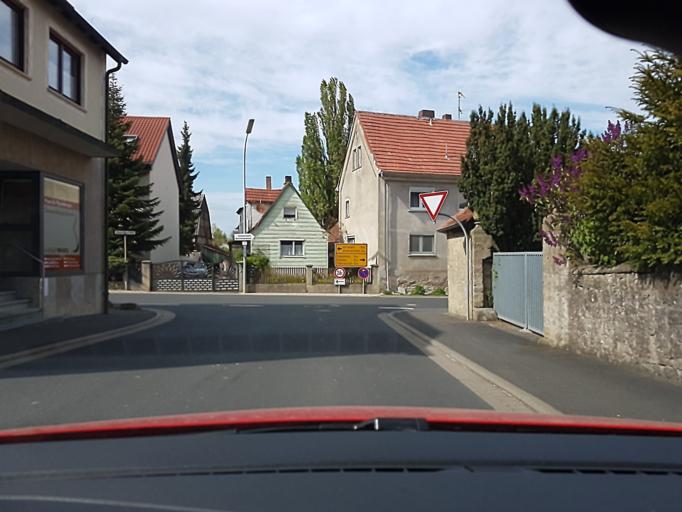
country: DE
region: Bavaria
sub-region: Regierungsbezirk Unterfranken
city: Bergtheim
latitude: 49.9253
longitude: 10.0261
